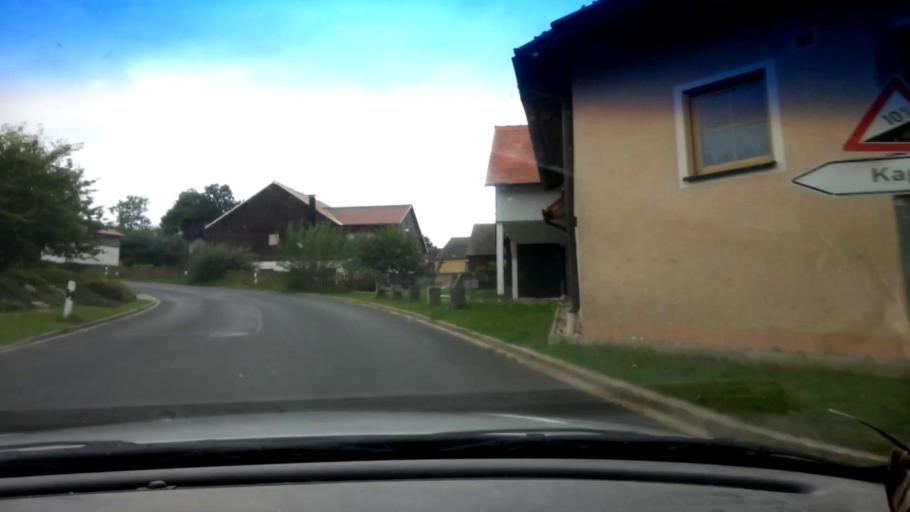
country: DE
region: Bavaria
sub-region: Upper Palatinate
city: Waldsassen
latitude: 50.0352
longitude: 12.2832
